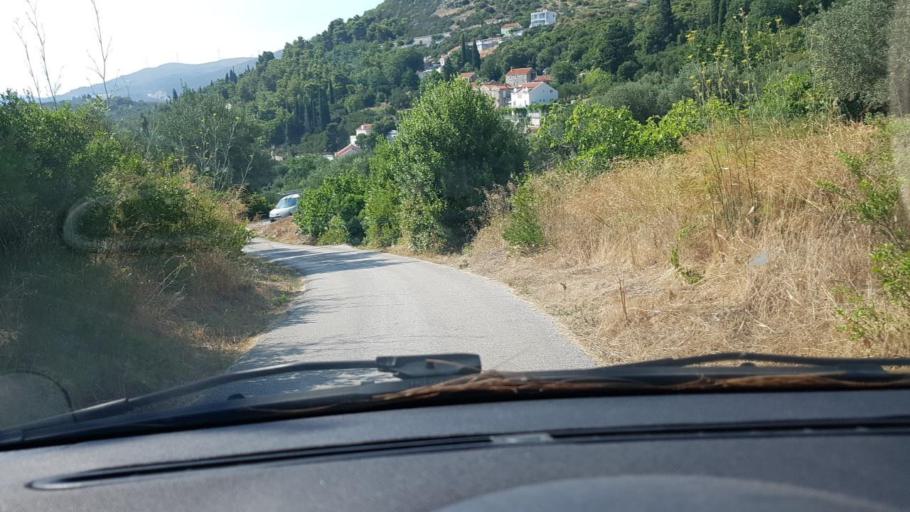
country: HR
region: Dubrovacko-Neretvanska
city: Podgora
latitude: 42.7828
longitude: 17.8624
